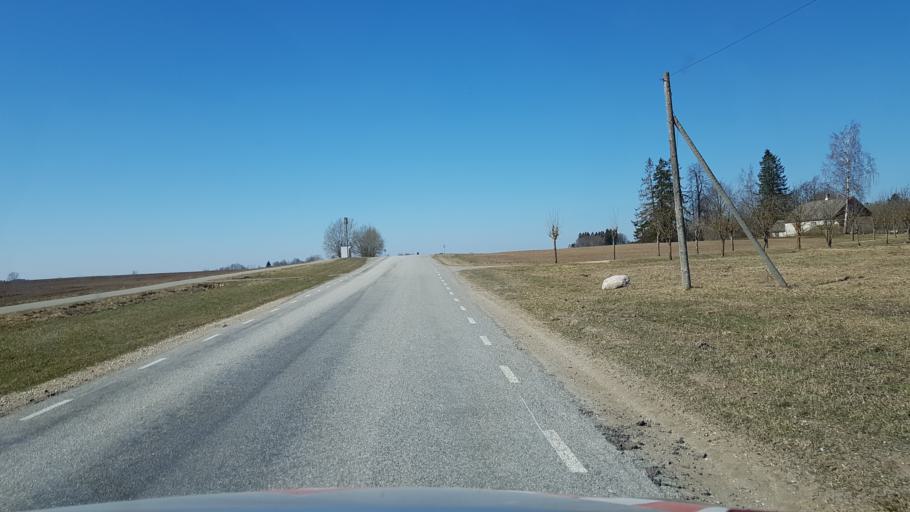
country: EE
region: Laeaene-Virumaa
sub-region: Vinni vald
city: Vinni
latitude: 59.0693
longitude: 26.5273
